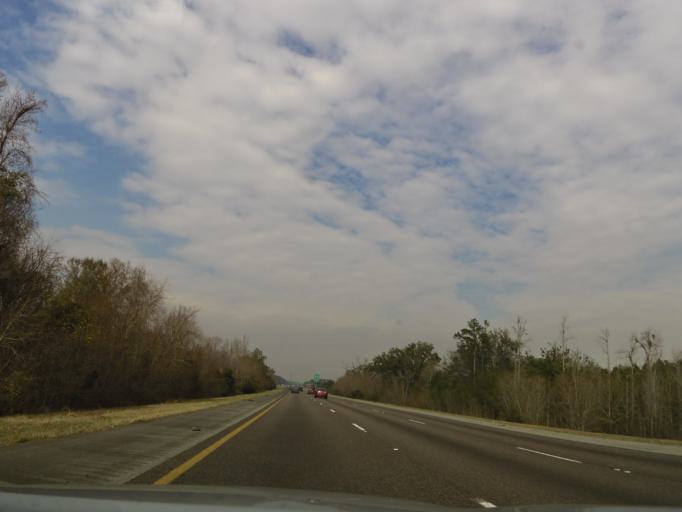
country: US
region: Georgia
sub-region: Liberty County
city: Midway
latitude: 31.7635
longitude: -81.3811
